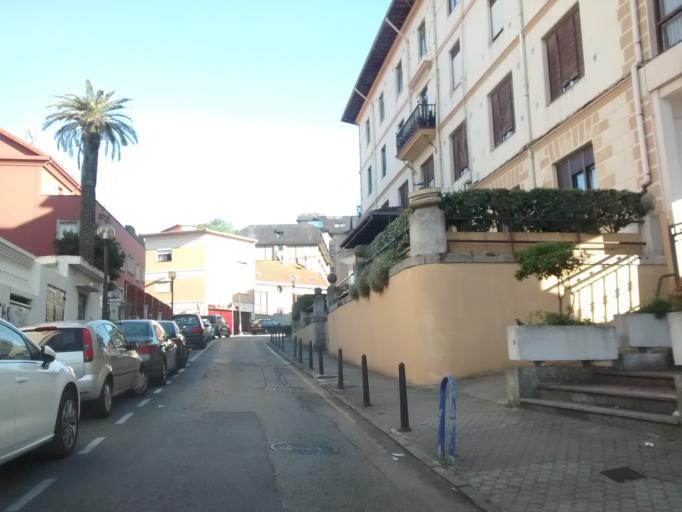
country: ES
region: Cantabria
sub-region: Provincia de Cantabria
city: Santander
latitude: 43.4717
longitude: -3.7834
